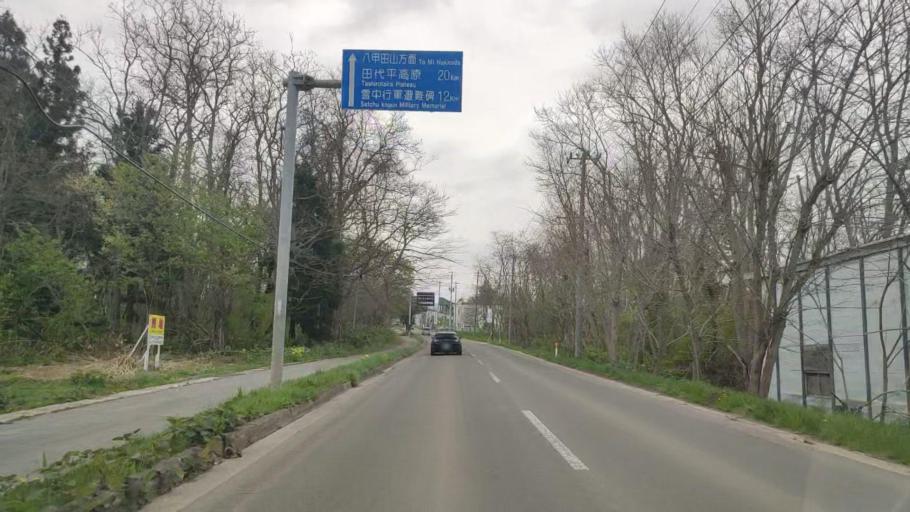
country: JP
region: Aomori
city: Aomori Shi
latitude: 40.7766
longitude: 140.7948
